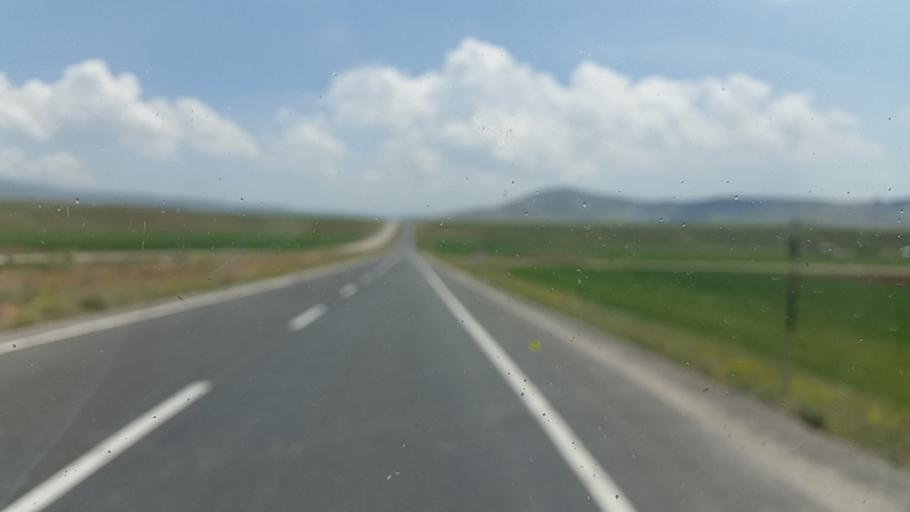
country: TR
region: Agri
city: Taslicay
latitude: 39.6282
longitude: 43.4435
